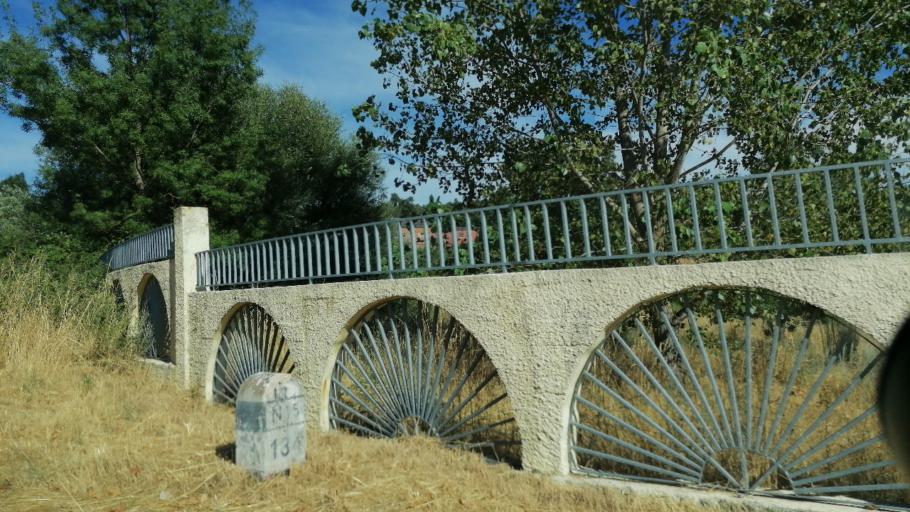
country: PT
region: Vila Real
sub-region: Murca
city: Murca
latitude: 41.3777
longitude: -7.5184
